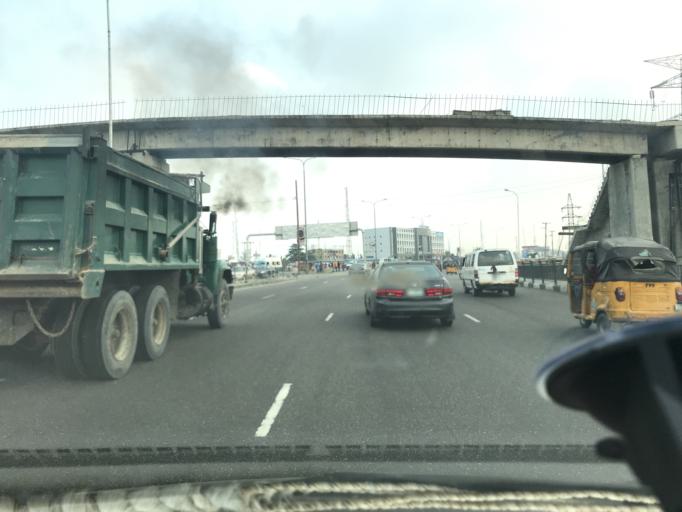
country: NG
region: Lagos
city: Ikoyi
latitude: 6.4613
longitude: 3.5557
